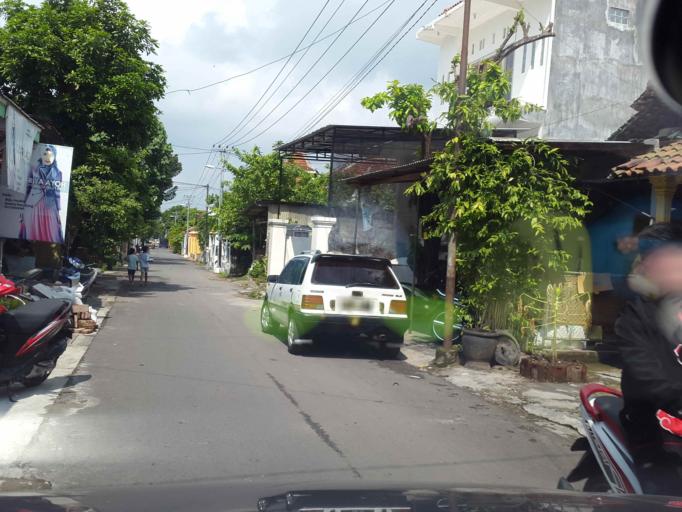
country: ID
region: East Java
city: Blitar
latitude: -8.1006
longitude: 112.1558
